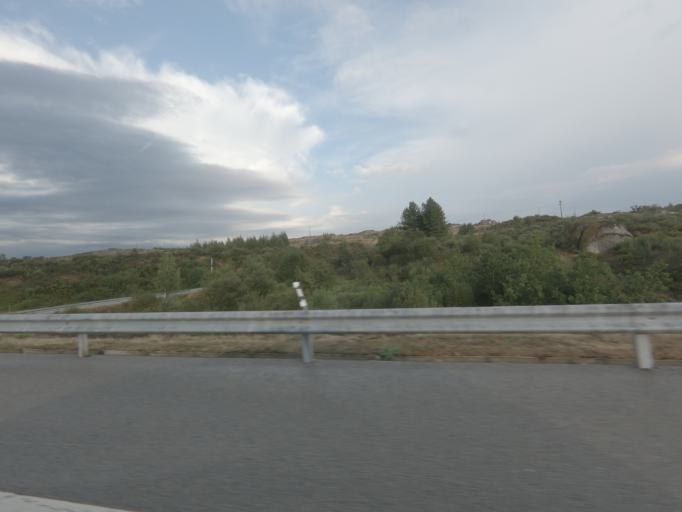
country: PT
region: Viseu
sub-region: Castro Daire
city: Castro Daire
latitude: 40.9744
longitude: -7.8869
